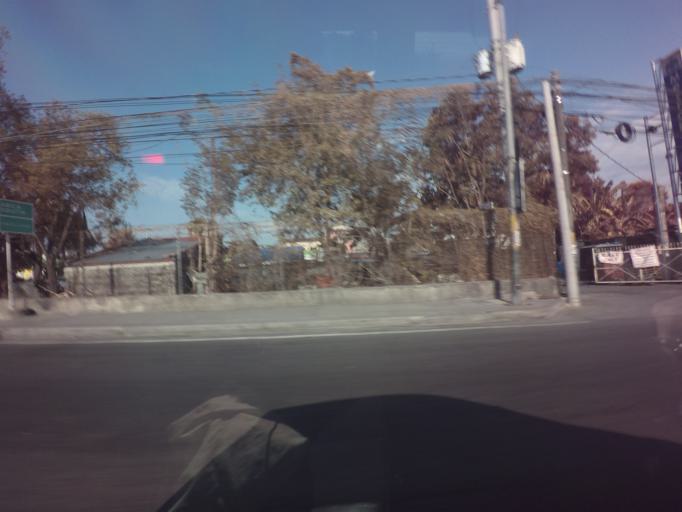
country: PH
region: Calabarzon
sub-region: Province of Rizal
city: Taguig
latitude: 14.4858
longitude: 121.0455
